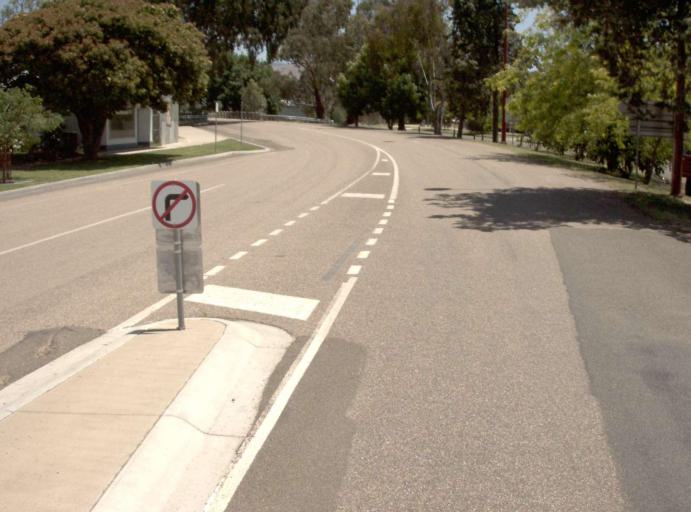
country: AU
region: Victoria
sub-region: East Gippsland
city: Bairnsdale
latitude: -37.2630
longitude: 147.7216
